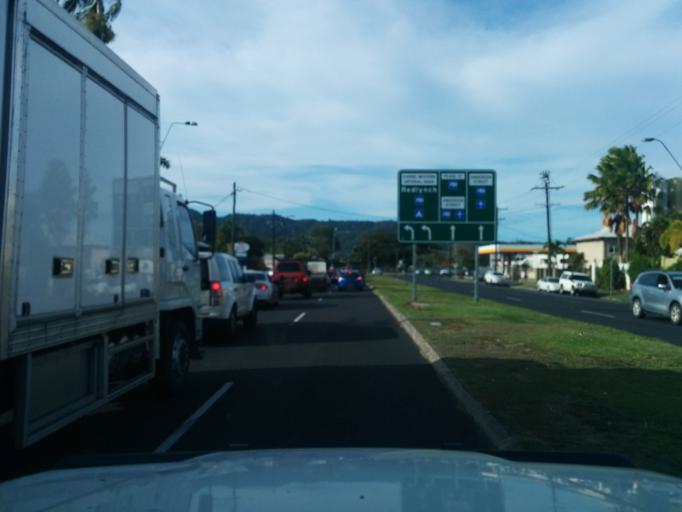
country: AU
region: Queensland
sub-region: Cairns
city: Cairns
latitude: -16.9200
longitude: 145.7403
